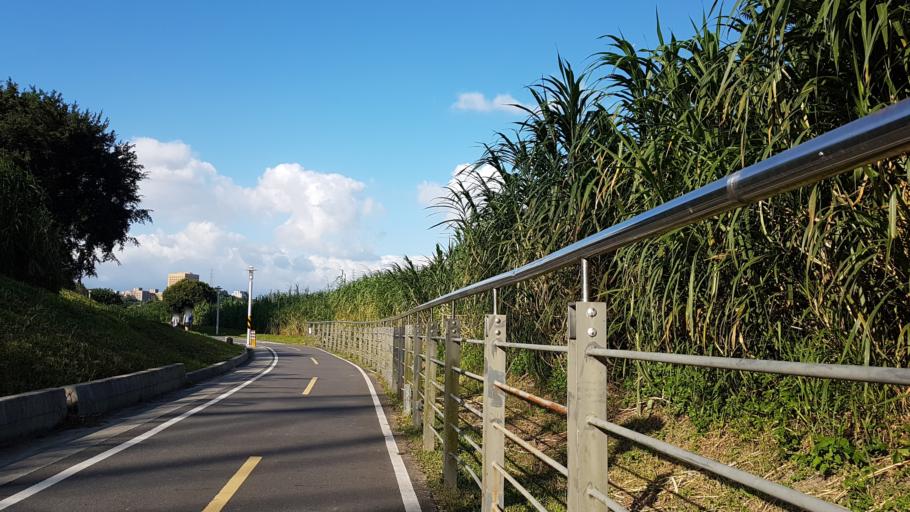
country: TW
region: Taipei
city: Taipei
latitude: 25.0020
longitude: 121.5313
